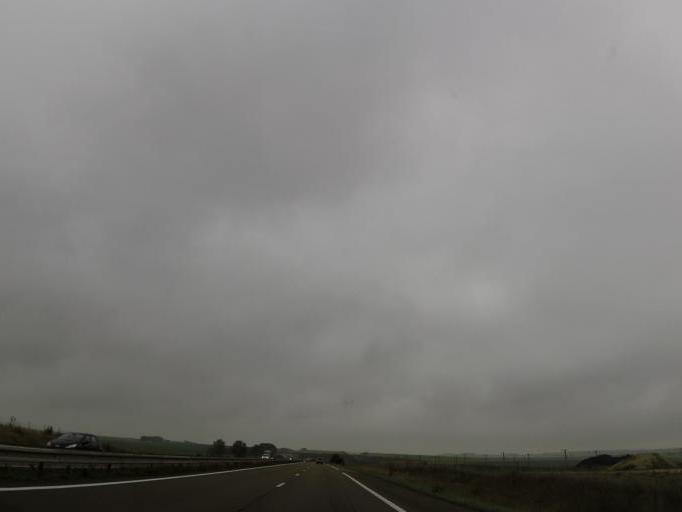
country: FR
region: Champagne-Ardenne
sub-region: Departement de la Marne
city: Verzy
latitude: 49.1551
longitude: 4.1988
